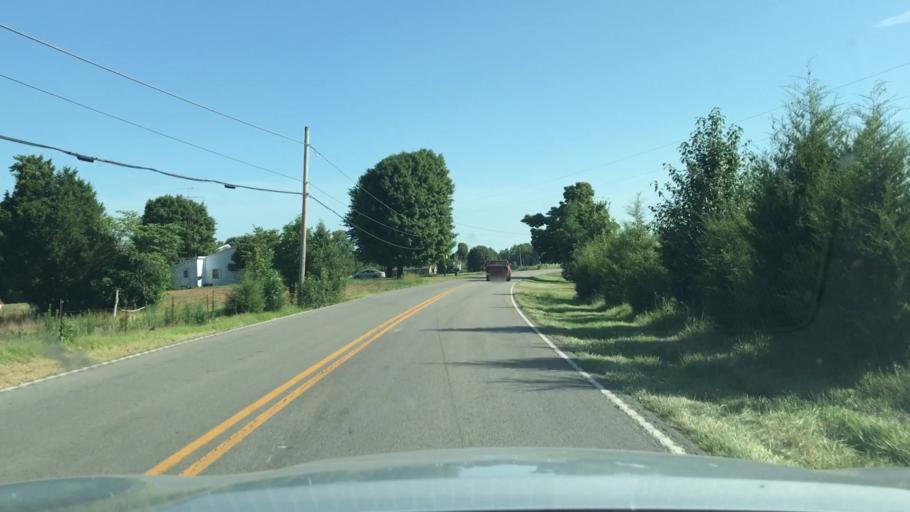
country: US
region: Kentucky
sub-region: Muhlenberg County
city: Greenville
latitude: 37.1748
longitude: -87.1529
